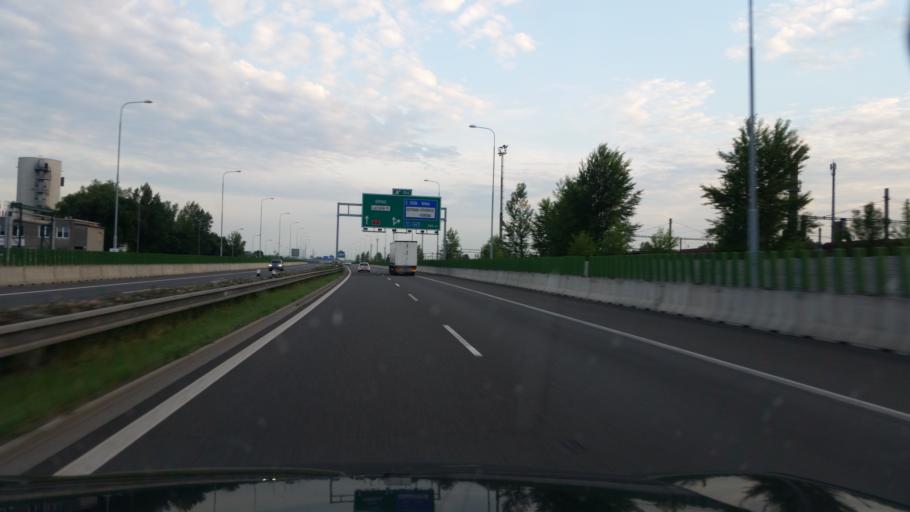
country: CZ
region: Moravskoslezsky
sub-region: Okres Ostrava-Mesto
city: Ostrava
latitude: 49.8212
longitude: 18.2114
